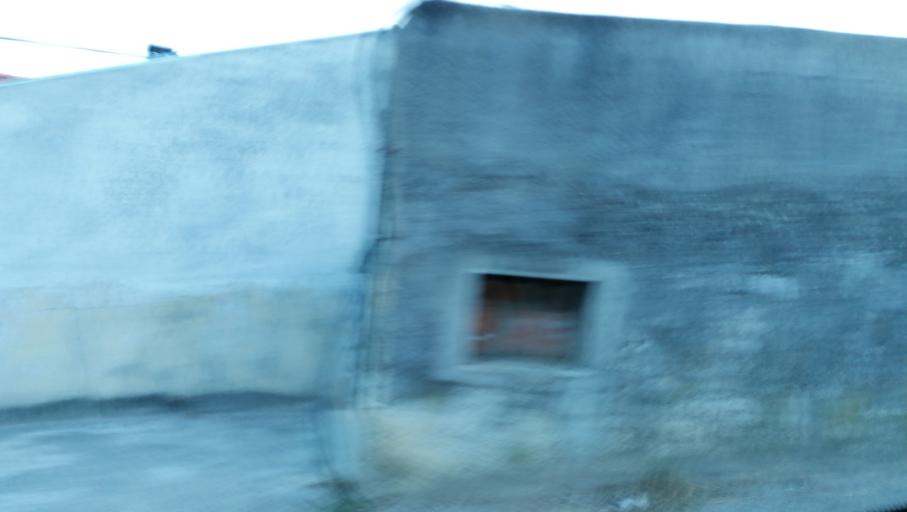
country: PT
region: Viseu
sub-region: Armamar
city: Armamar
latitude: 41.1597
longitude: -7.6838
